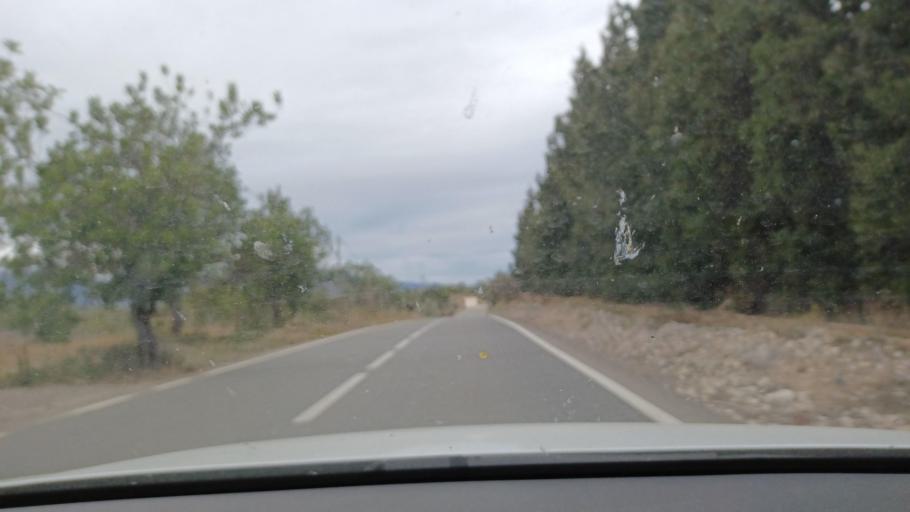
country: ES
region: Catalonia
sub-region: Provincia de Tarragona
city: Ulldecona
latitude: 40.6122
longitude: 0.3500
